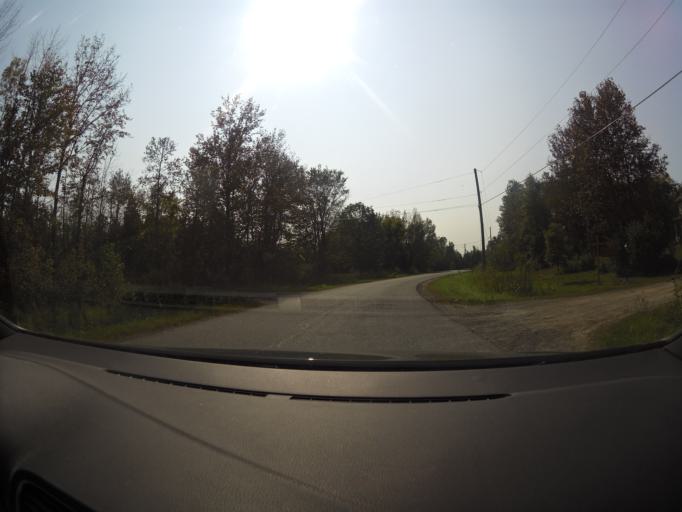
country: CA
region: Ontario
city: Carleton Place
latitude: 45.3287
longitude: -76.1585
